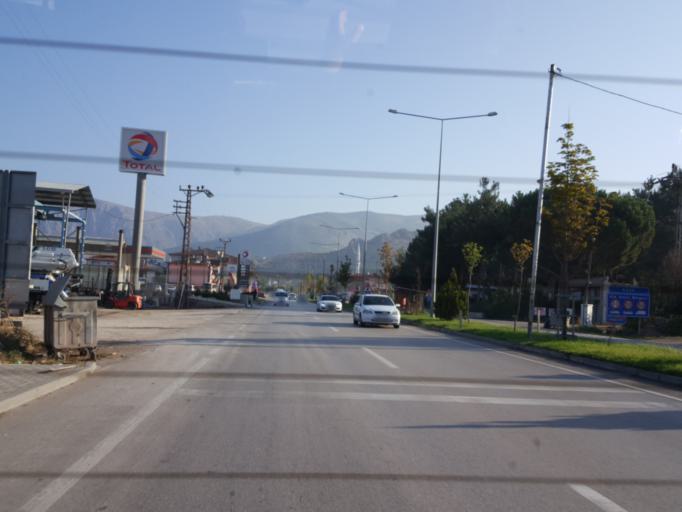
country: TR
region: Amasya
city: Amasya
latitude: 40.5991
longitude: 35.8073
